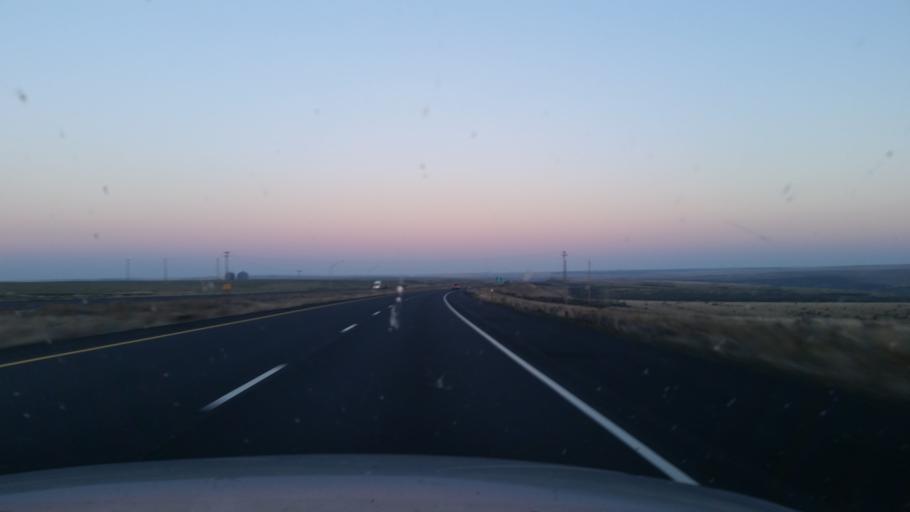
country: US
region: Washington
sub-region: Adams County
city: Ritzville
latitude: 47.0967
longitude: -118.6815
